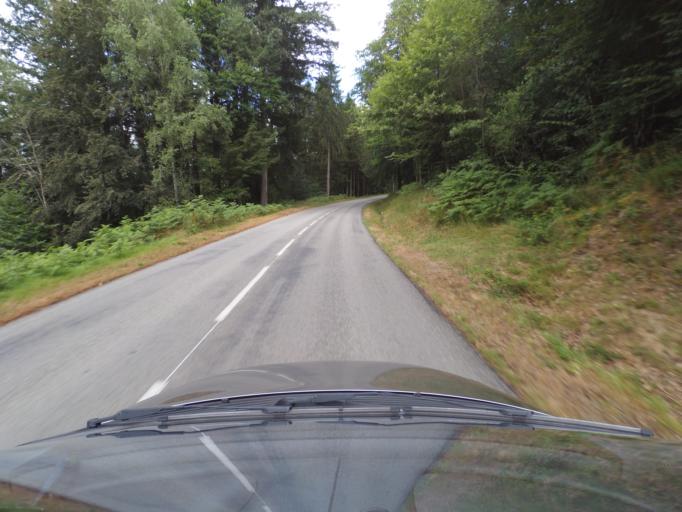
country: FR
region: Limousin
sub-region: Departement de la Creuse
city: Bourganeuf
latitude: 45.8980
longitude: 1.8605
